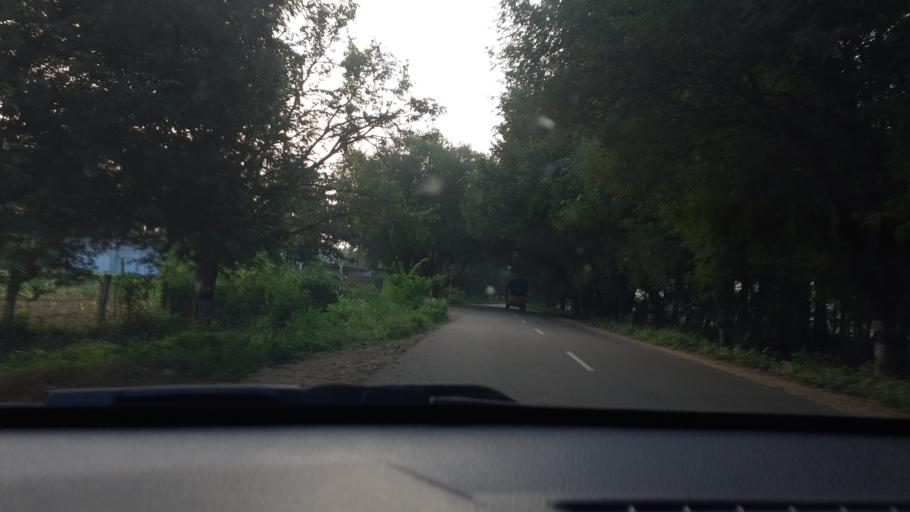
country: IN
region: Tamil Nadu
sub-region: Dindigul
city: Palani
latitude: 10.4285
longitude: 77.5308
